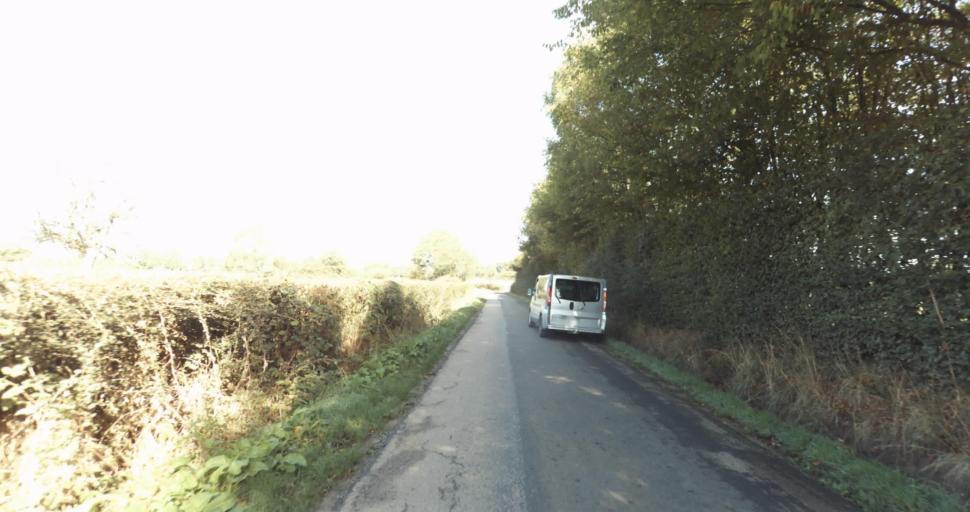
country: FR
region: Lower Normandy
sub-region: Departement de l'Orne
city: Vimoutiers
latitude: 48.9150
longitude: 0.3037
